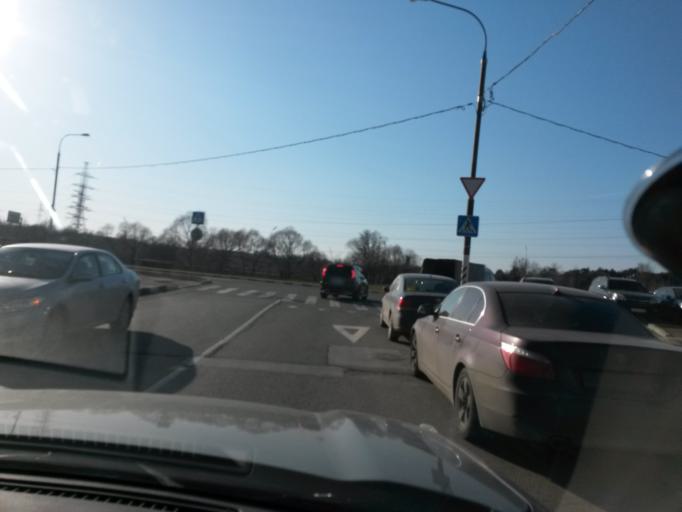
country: RU
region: Moscow
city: Chertanovo Yuzhnoye
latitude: 55.5761
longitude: 37.5692
